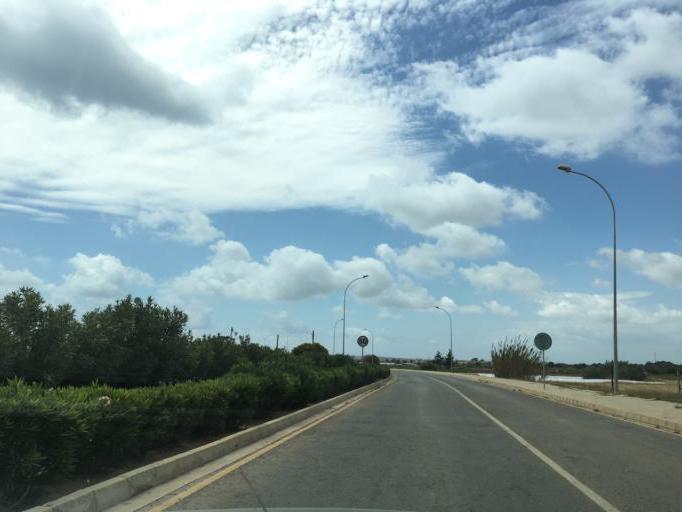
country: CY
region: Ammochostos
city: Liopetri
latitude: 34.9834
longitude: 33.9410
